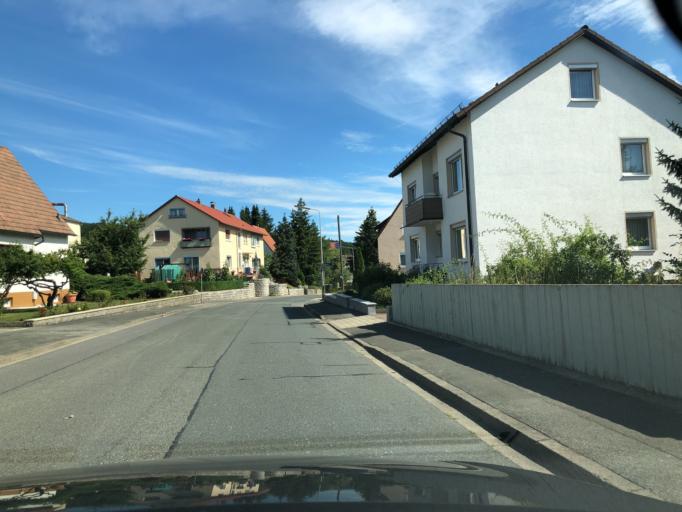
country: DE
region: Bavaria
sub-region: Upper Franconia
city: Sonnefeld
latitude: 50.2140
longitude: 11.0885
